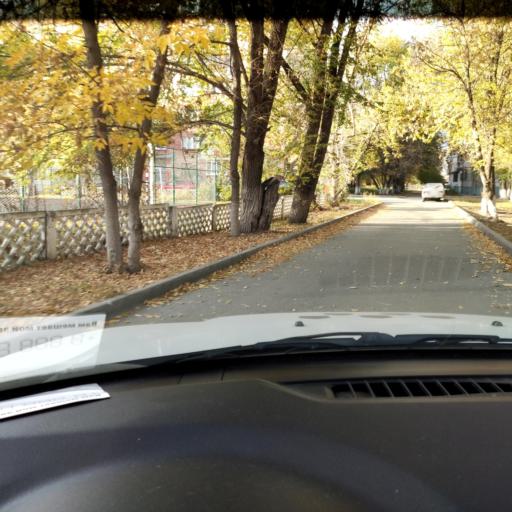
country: RU
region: Samara
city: Tol'yatti
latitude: 53.5002
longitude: 49.4067
